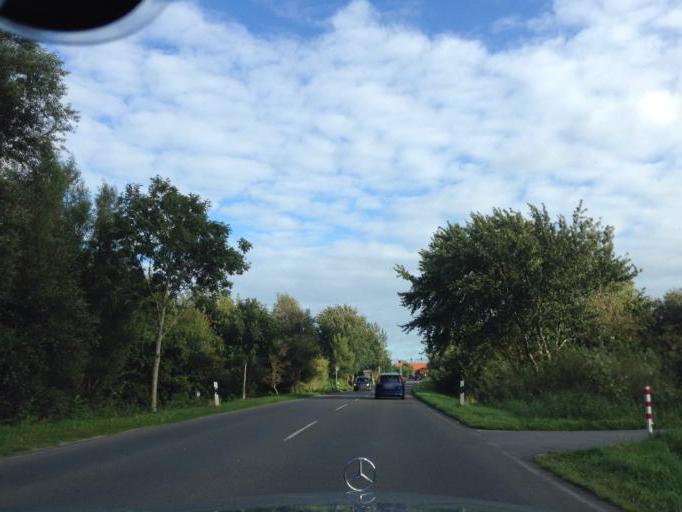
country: DE
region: Schleswig-Holstein
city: Wyk auf Fohr
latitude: 54.6942
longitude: 8.5655
